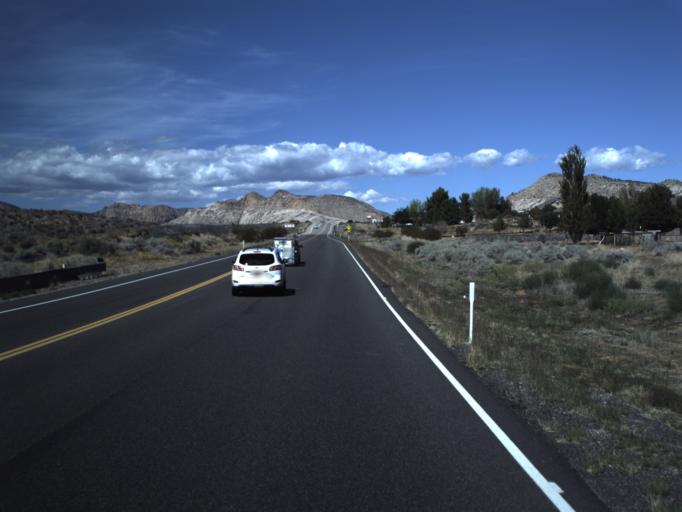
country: US
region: Utah
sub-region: Washington County
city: Ivins
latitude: 37.2015
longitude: -113.6257
